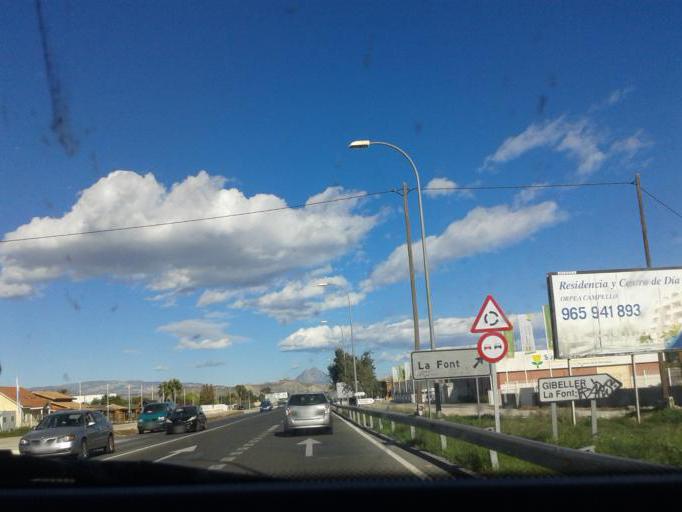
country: ES
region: Valencia
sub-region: Provincia de Alicante
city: el Campello
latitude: 38.4162
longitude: -0.4168
